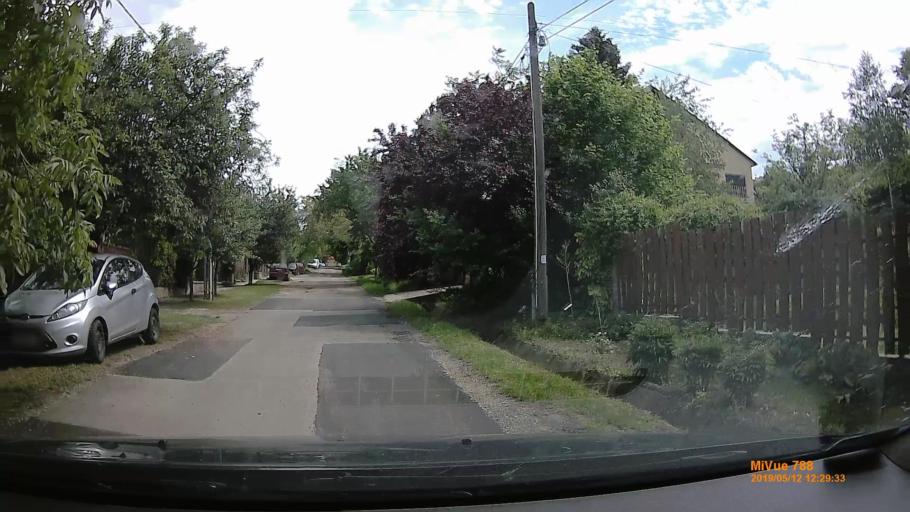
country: HU
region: Pest
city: Ecser
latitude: 47.4575
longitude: 19.3041
